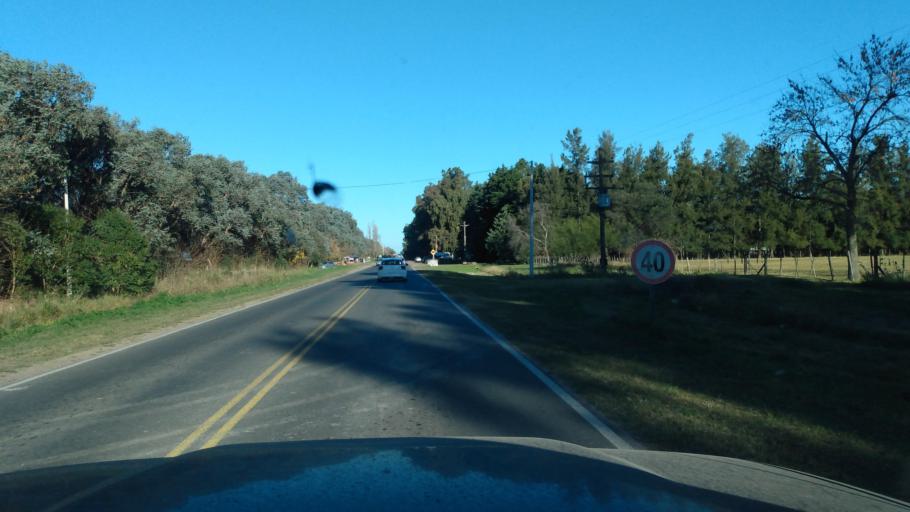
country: AR
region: Buenos Aires
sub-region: Partido de Lujan
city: Lujan
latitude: -34.5279
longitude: -59.1700
